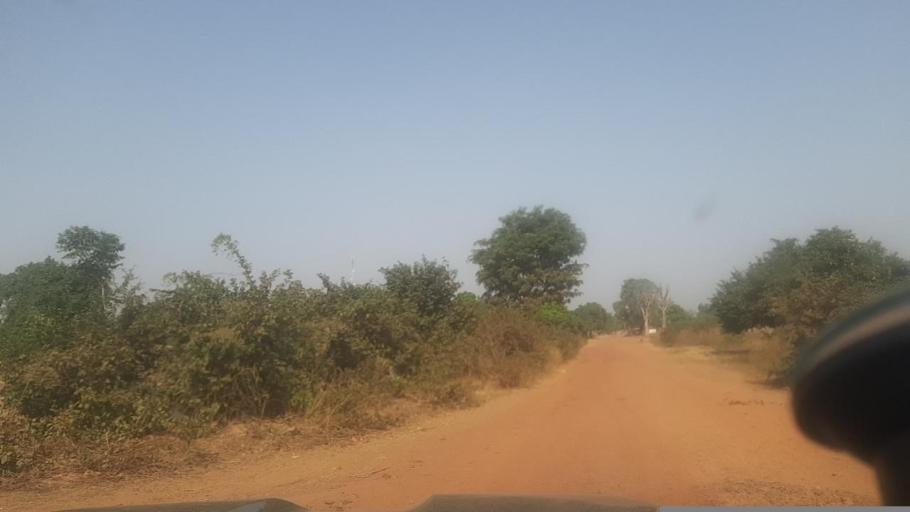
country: ML
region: Segou
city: Bla
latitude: 12.8456
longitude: -5.9941
